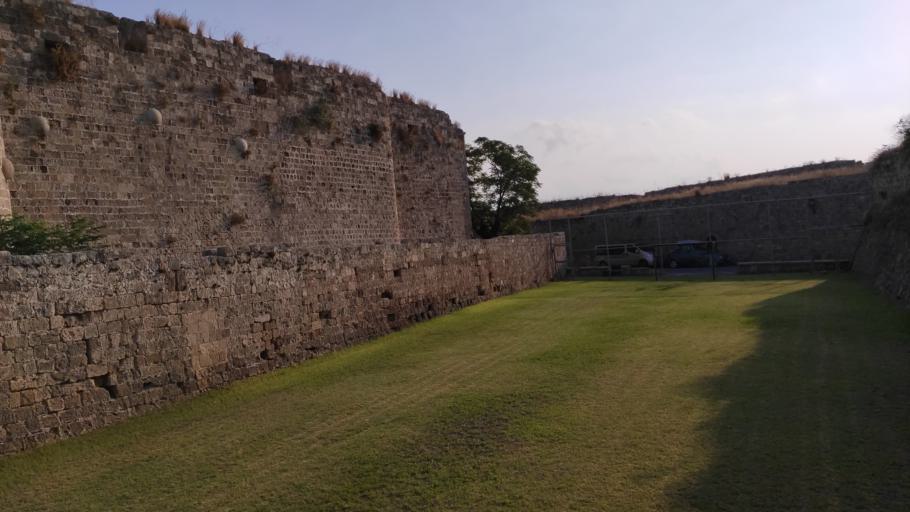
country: GR
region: South Aegean
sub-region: Nomos Dodekanisou
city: Rodos
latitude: 36.4419
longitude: 28.2325
